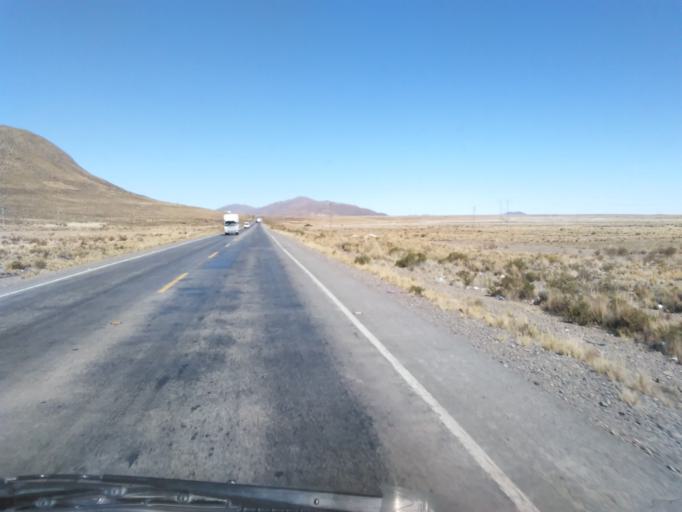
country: BO
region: Oruro
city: Machacamarca
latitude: -18.1102
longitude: -67.0053
